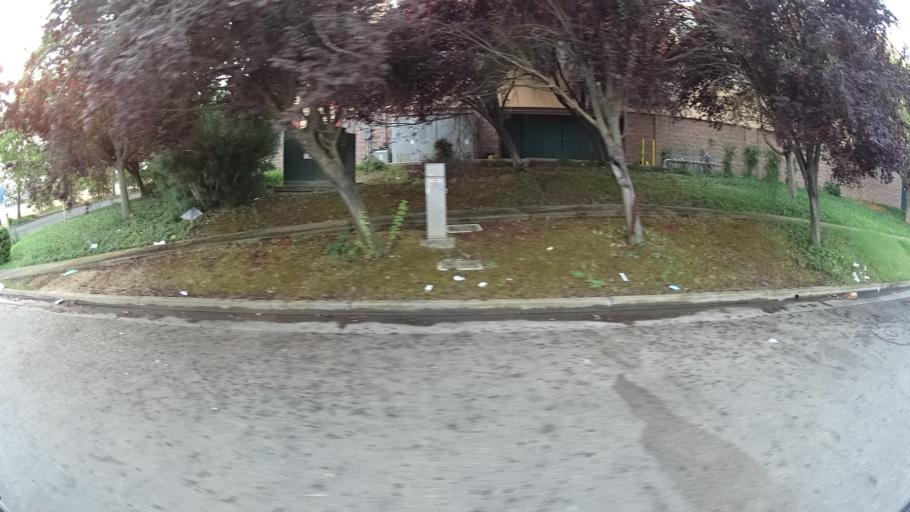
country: US
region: California
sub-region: Sacramento County
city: Laguna
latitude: 38.4189
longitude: -121.4042
